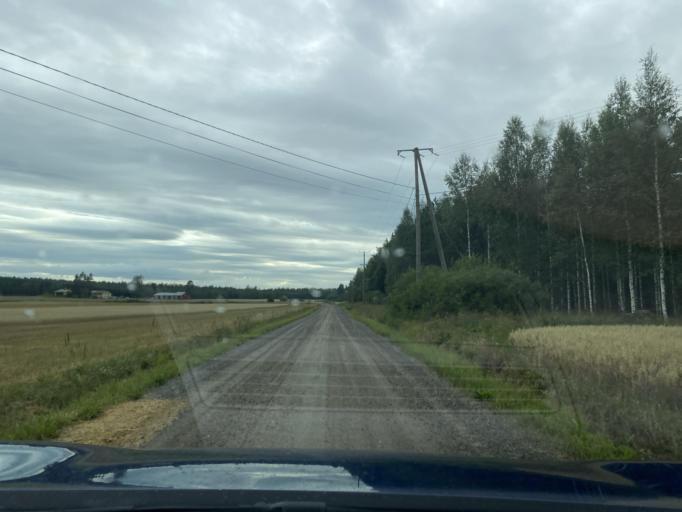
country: FI
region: Pirkanmaa
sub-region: Lounais-Pirkanmaa
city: Punkalaidun
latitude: 61.2354
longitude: 23.0453
